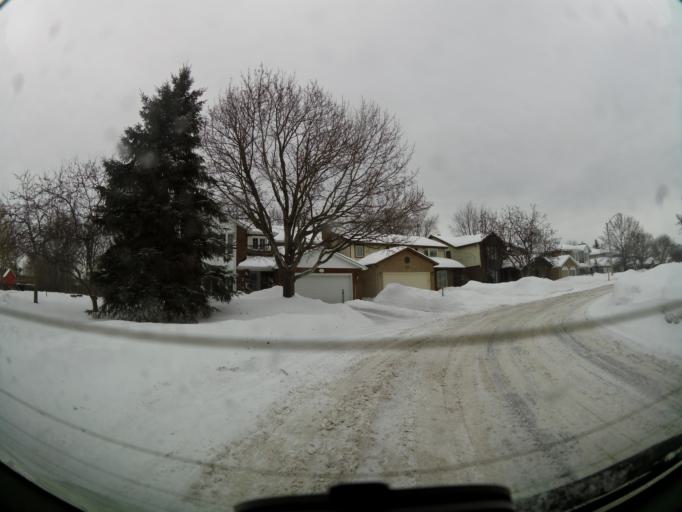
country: CA
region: Ontario
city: Ottawa
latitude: 45.3740
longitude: -75.6144
